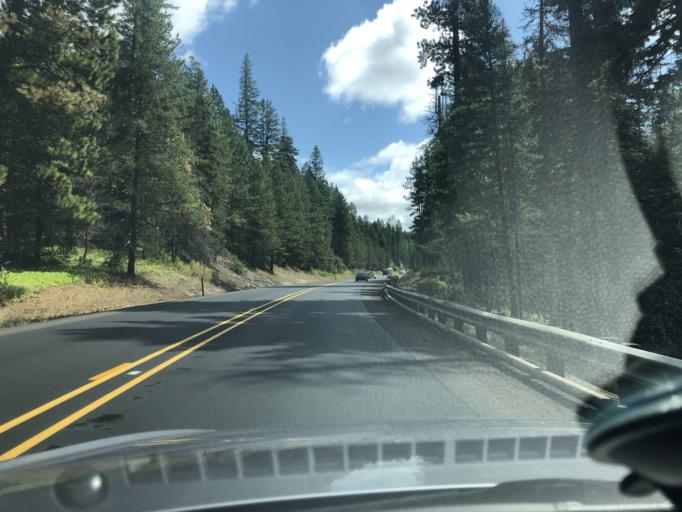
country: US
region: Washington
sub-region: Chelan County
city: Cashmere
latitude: 47.3352
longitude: -120.6275
